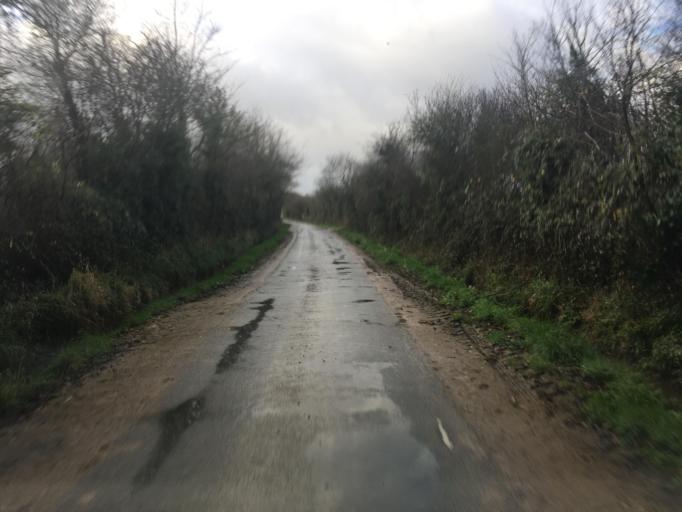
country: FR
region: Lower Normandy
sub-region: Departement de la Manche
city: Saint-Pierre-Eglise
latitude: 49.6726
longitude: -1.3224
